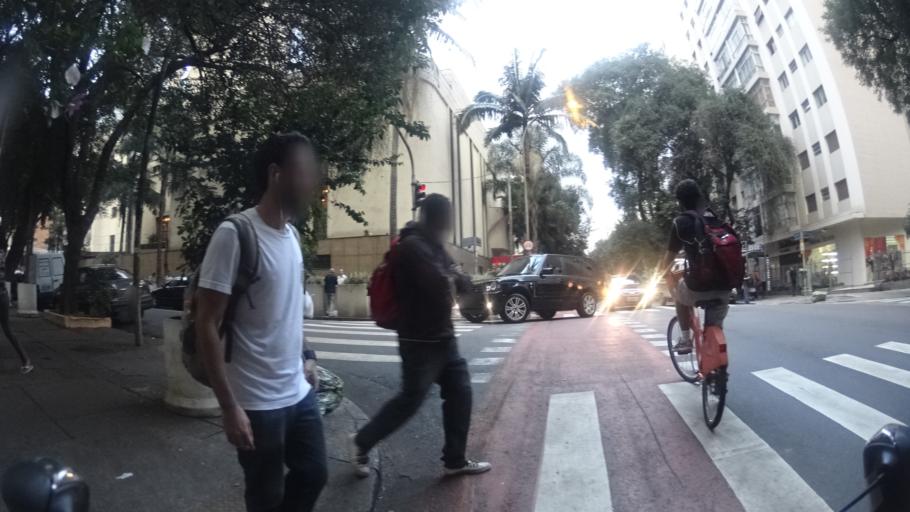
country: BR
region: Sao Paulo
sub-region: Sao Paulo
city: Sao Paulo
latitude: -23.5367
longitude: -46.6555
